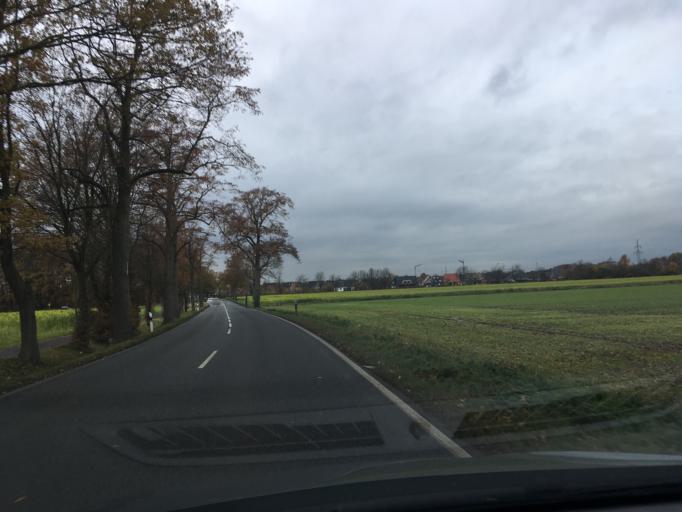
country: DE
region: North Rhine-Westphalia
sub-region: Regierungsbezirk Munster
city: Ahaus
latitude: 52.0887
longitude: 6.9911
